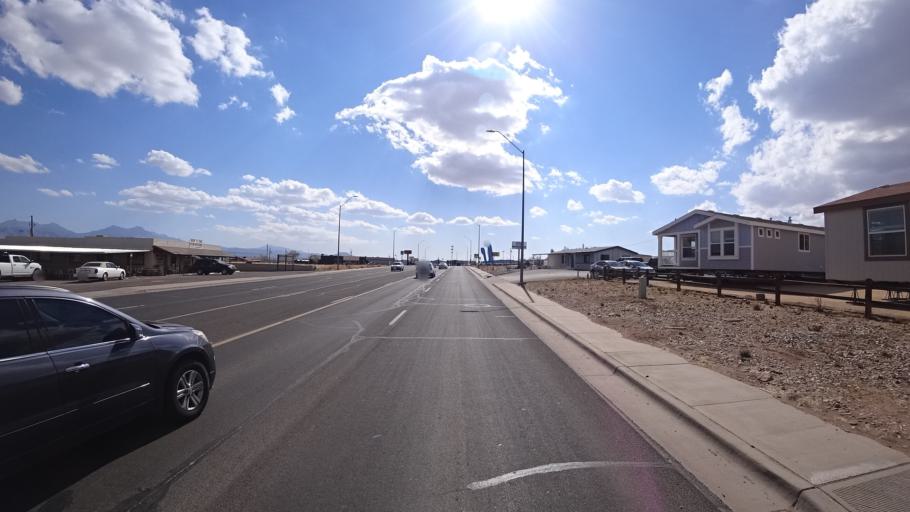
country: US
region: Arizona
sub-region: Mohave County
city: New Kingman-Butler
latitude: 35.2530
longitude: -114.0383
